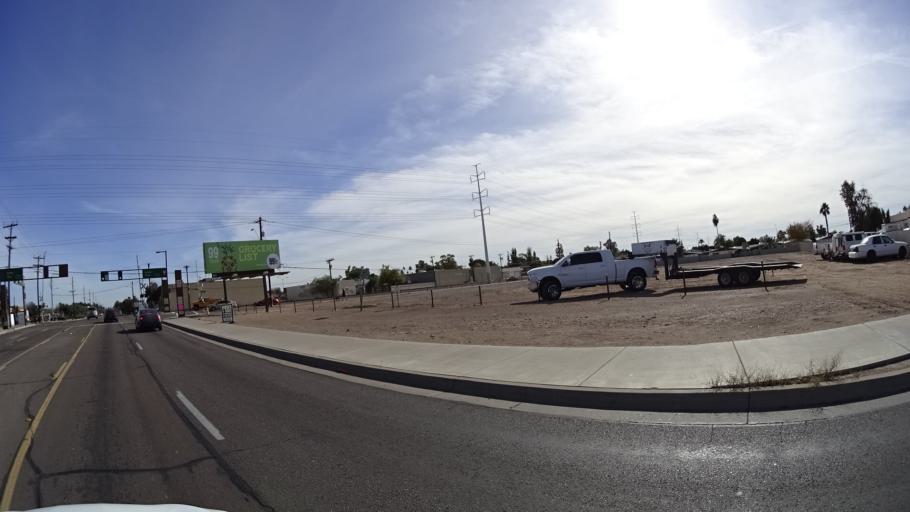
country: US
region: Arizona
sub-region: Maricopa County
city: Tempe Junction
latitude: 33.3928
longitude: -111.9445
